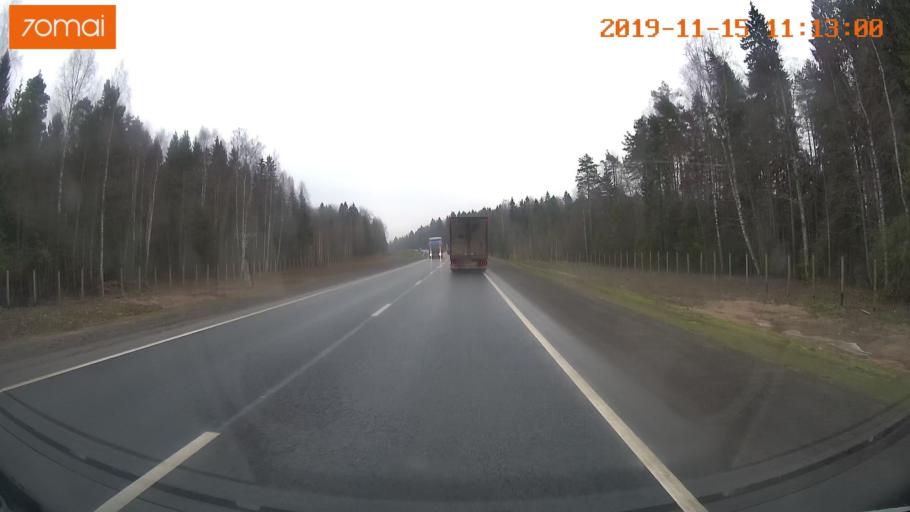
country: RU
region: Vologda
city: Chebsara
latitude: 59.1216
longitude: 39.1600
